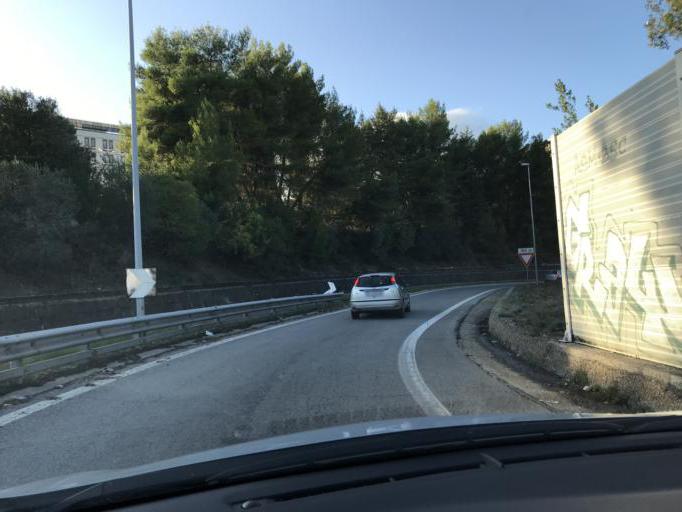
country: IT
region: Umbria
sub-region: Provincia di Perugia
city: Perugia
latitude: 43.0977
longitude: 12.3675
